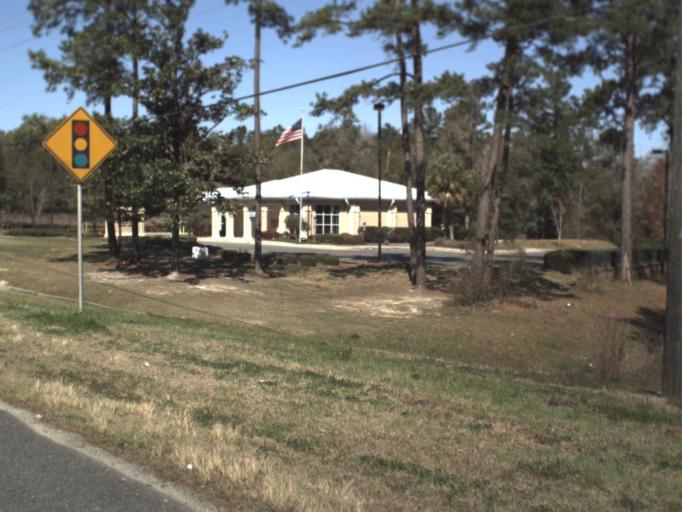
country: US
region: Florida
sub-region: Jackson County
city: Marianna
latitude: 30.7481
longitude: -85.1848
